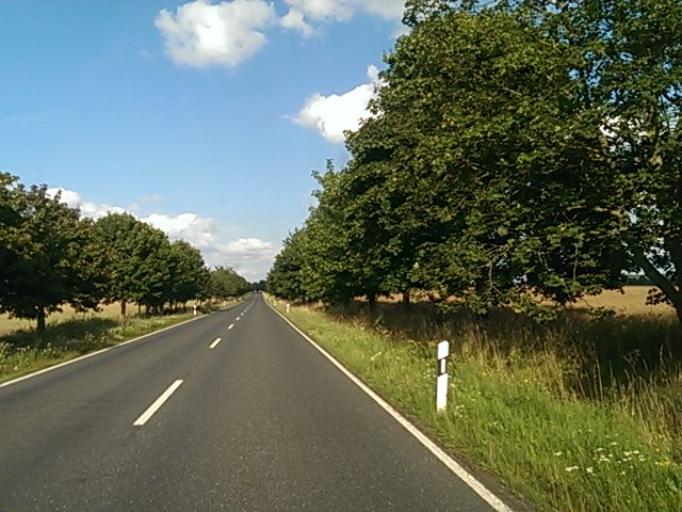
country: DE
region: Saxony-Anhalt
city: Coswig
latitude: 51.9556
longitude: 12.4696
